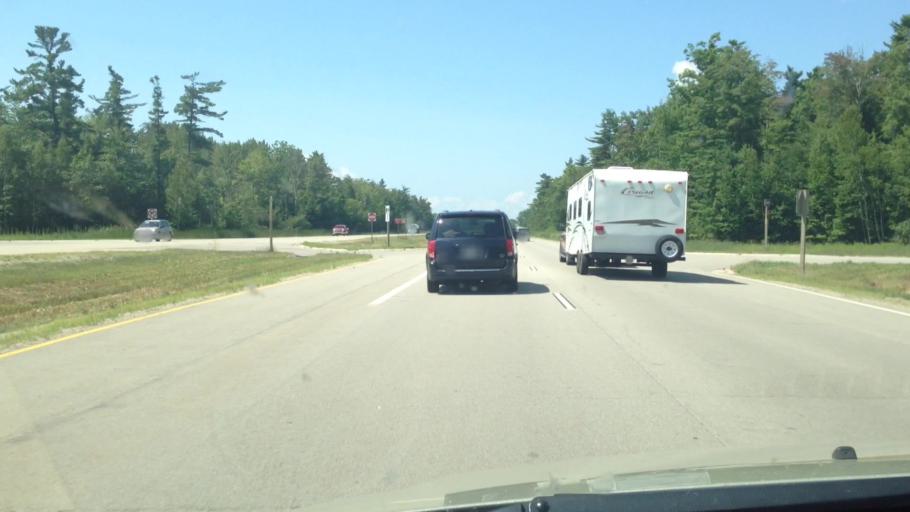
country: US
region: Wisconsin
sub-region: Oconto County
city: Oconto
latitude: 44.8085
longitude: -87.9662
